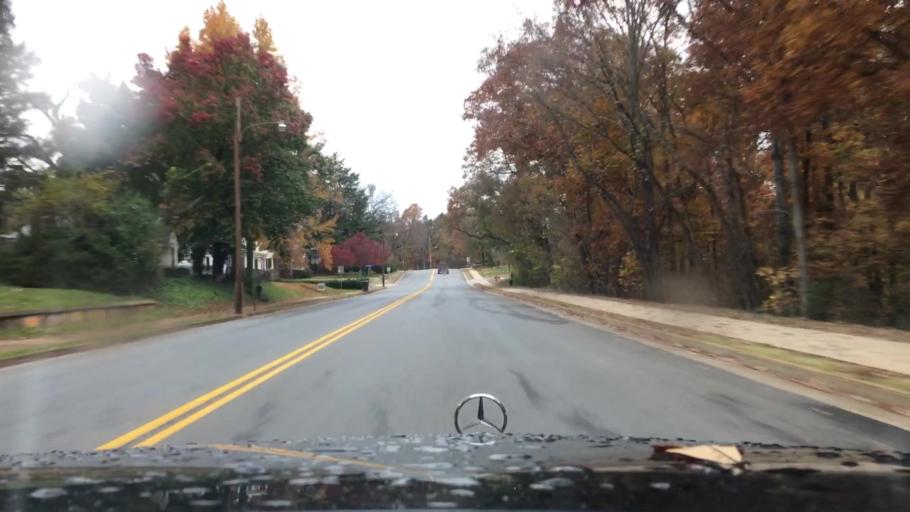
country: US
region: Virginia
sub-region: Campbell County
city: Altavista
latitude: 37.1147
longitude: -79.2993
